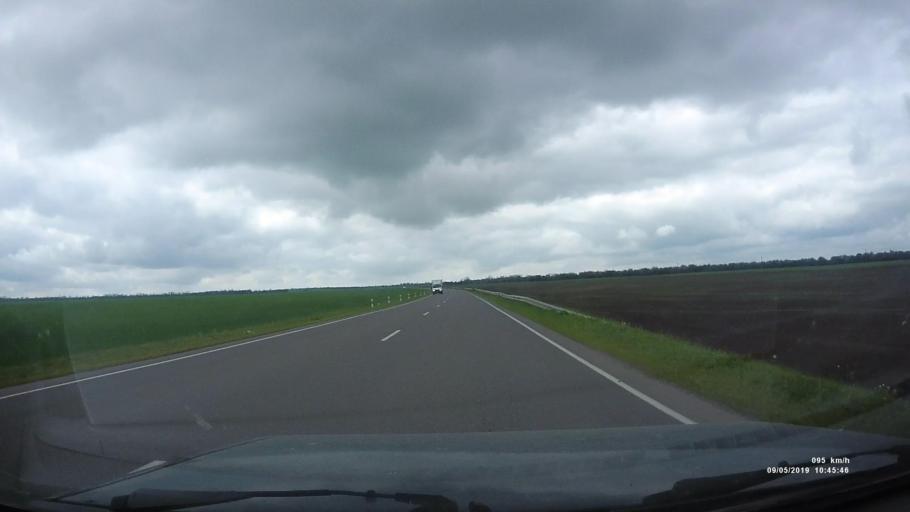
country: RU
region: Rostov
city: Peshkovo
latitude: 46.9925
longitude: 39.3626
